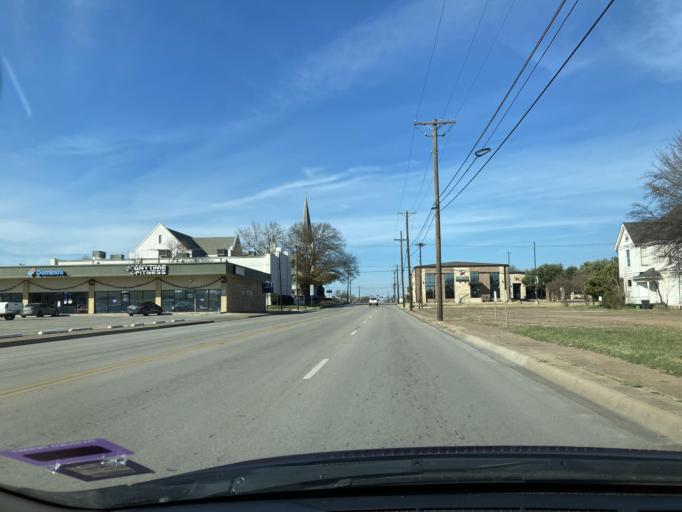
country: US
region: Texas
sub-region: Navarro County
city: Corsicana
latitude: 32.0920
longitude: -96.4698
